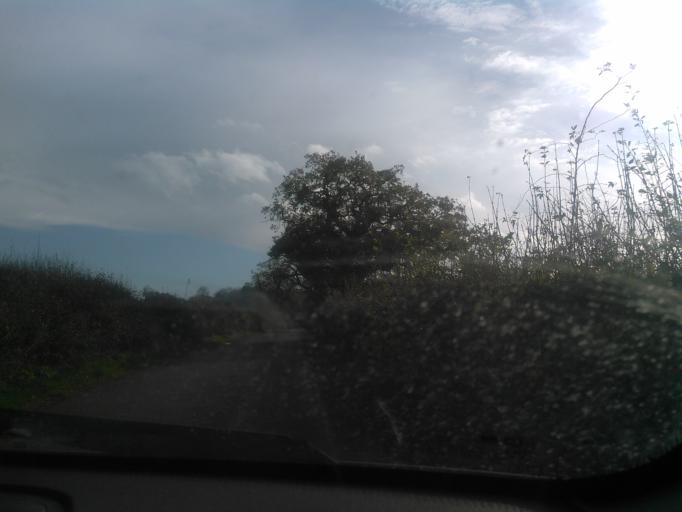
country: GB
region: England
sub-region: Shropshire
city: Wem
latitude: 52.8477
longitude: -2.7079
